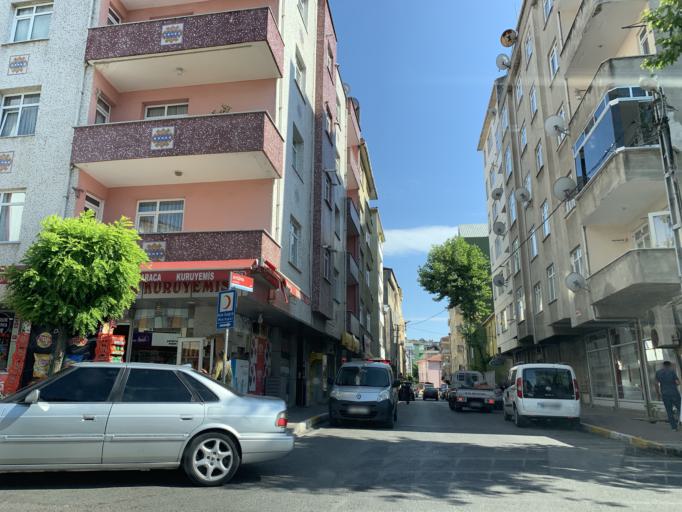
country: TR
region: Istanbul
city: Pendik
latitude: 40.8789
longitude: 29.2726
